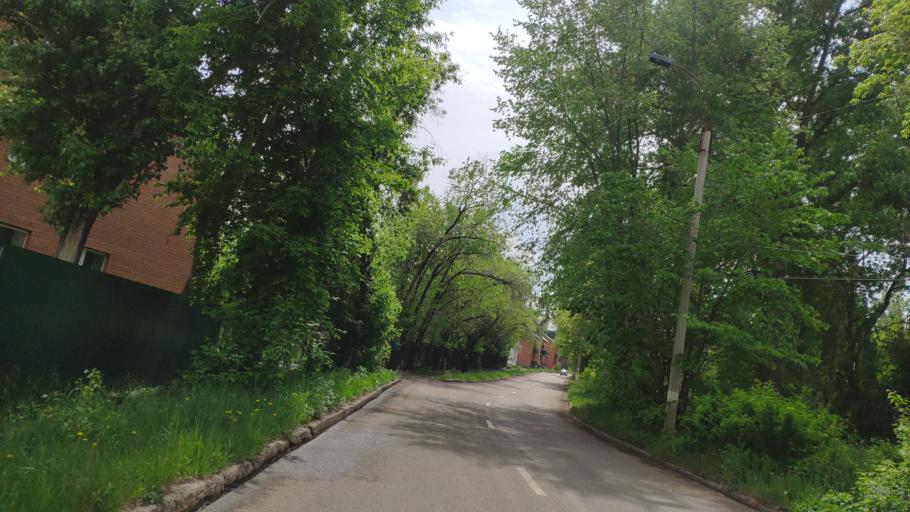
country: RU
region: Chelyabinsk
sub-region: Gorod Magnitogorsk
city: Magnitogorsk
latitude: 53.4204
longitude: 58.9563
